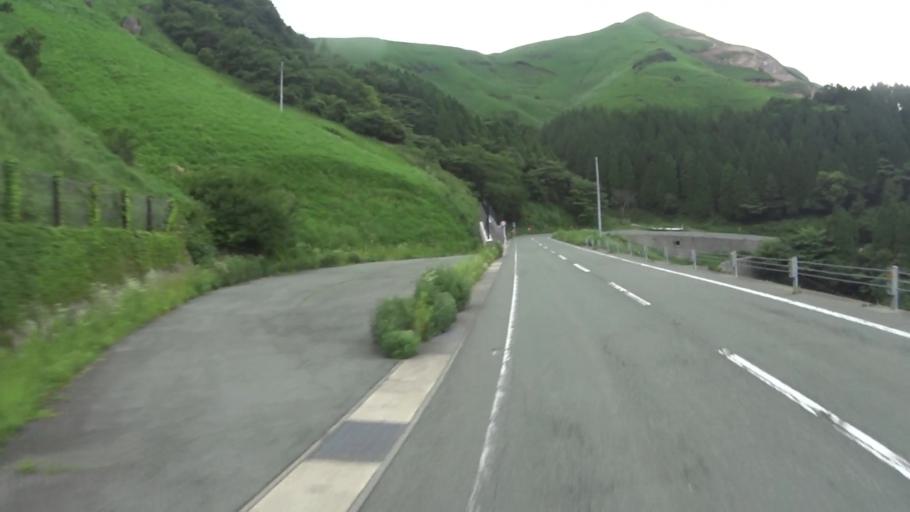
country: JP
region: Kumamoto
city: Aso
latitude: 32.9171
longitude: 130.9700
